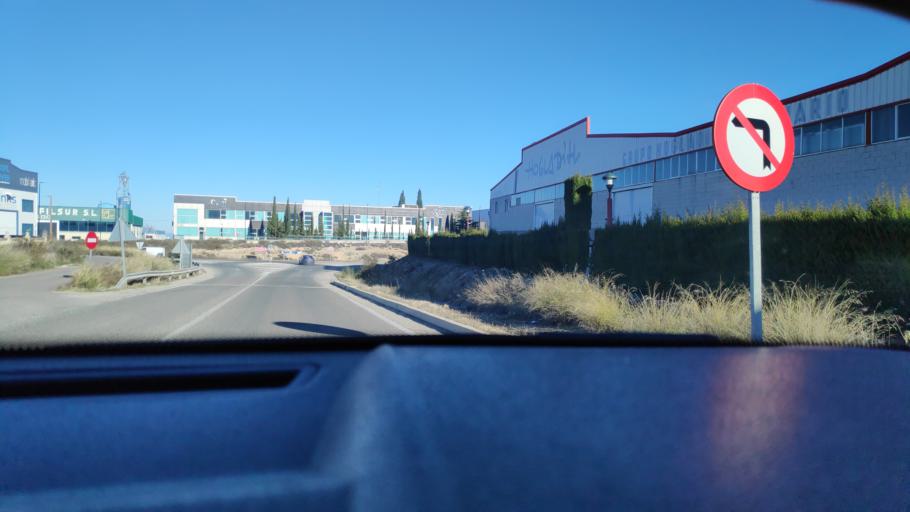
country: ES
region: Andalusia
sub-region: Provincia de Jaen
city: Mancha Real
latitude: 37.8062
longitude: -3.6118
